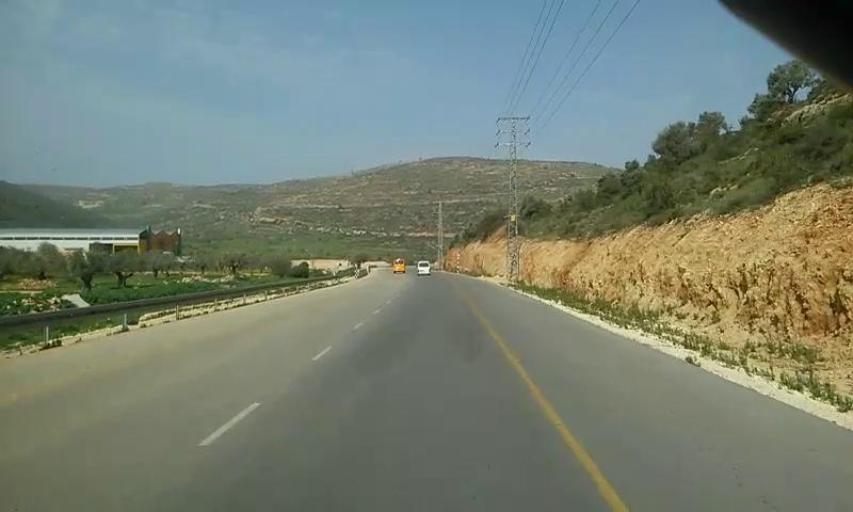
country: PS
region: West Bank
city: Dura al Qar`
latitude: 31.9858
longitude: 35.2296
